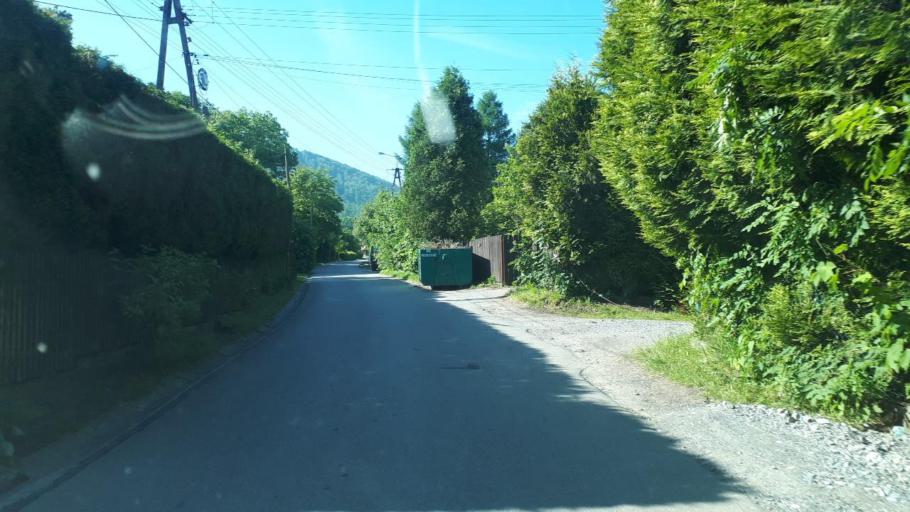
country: PL
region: Silesian Voivodeship
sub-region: Powiat bielski
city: Jaworze
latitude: 49.7884
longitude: 18.9449
